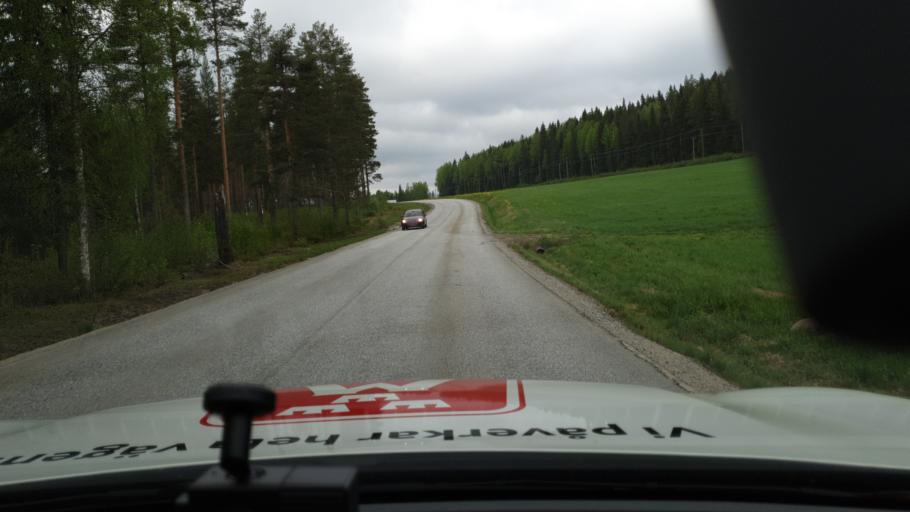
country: SE
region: Vaesterbotten
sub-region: Vindelns Kommun
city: Vindeln
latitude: 64.1785
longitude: 19.7235
